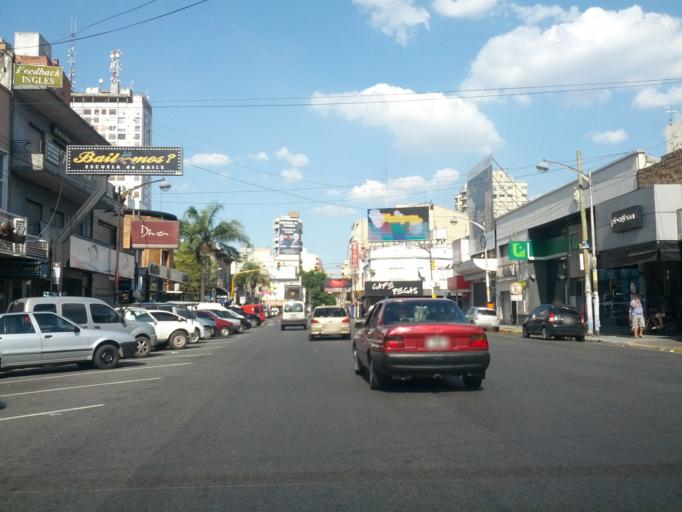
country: AR
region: Buenos Aires
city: San Justo
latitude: -34.6417
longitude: -58.5649
